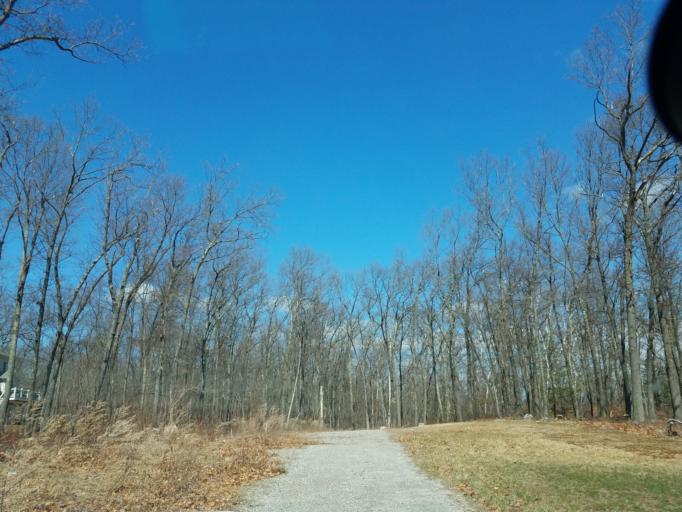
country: US
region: Connecticut
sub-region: Hartford County
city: Collinsville
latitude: 41.8051
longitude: -72.9000
